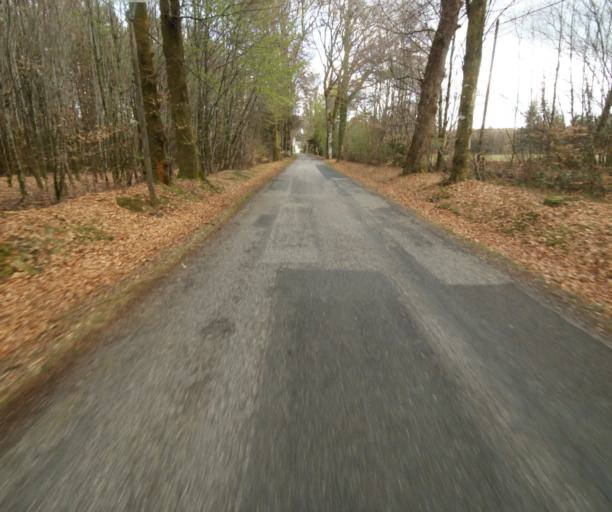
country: FR
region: Limousin
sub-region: Departement de la Correze
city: Correze
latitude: 45.2597
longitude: 1.9107
